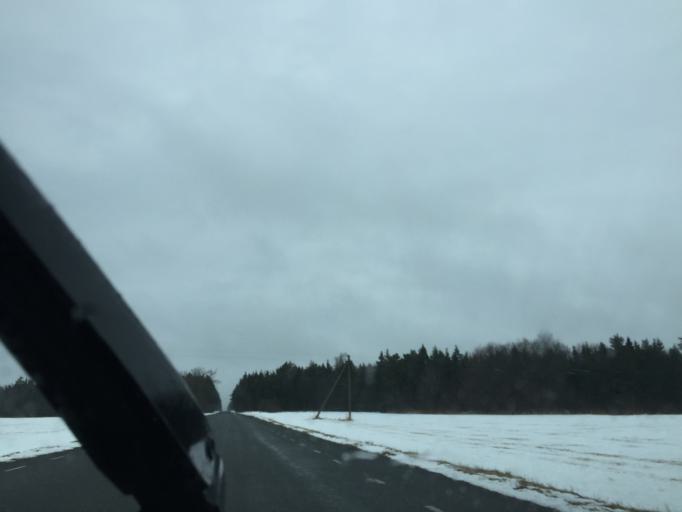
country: EE
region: Saare
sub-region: Kuressaare linn
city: Kuressaare
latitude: 58.3310
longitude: 22.0256
